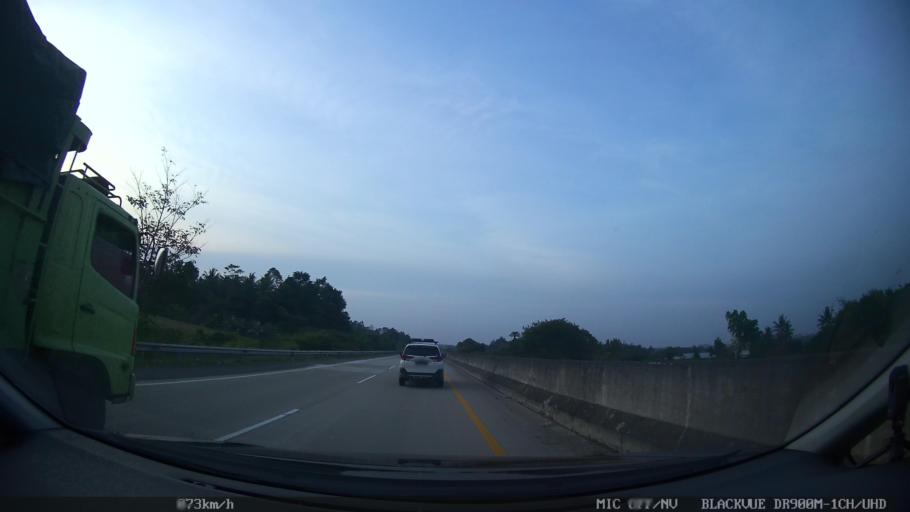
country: ID
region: Lampung
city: Penengahan
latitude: -5.7706
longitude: 105.7161
